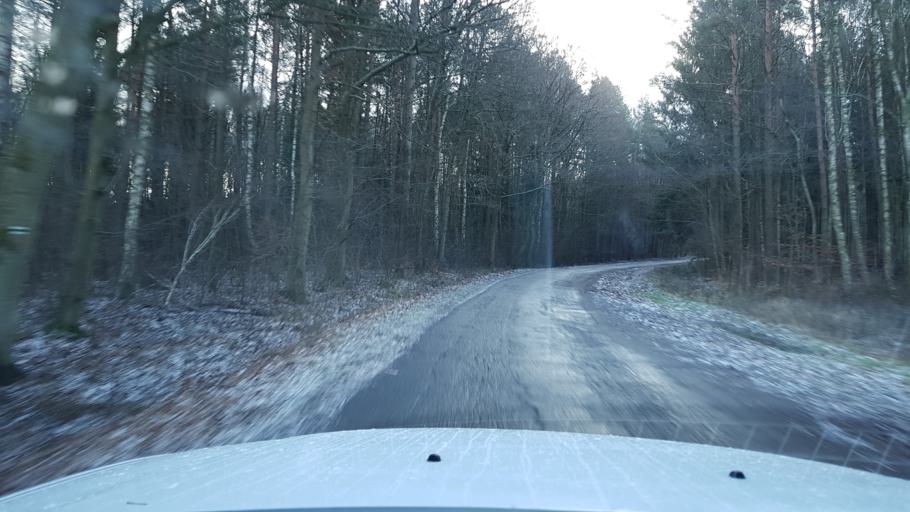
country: PL
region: West Pomeranian Voivodeship
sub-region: Powiat gryficki
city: Trzebiatow
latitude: 54.0457
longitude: 15.3272
